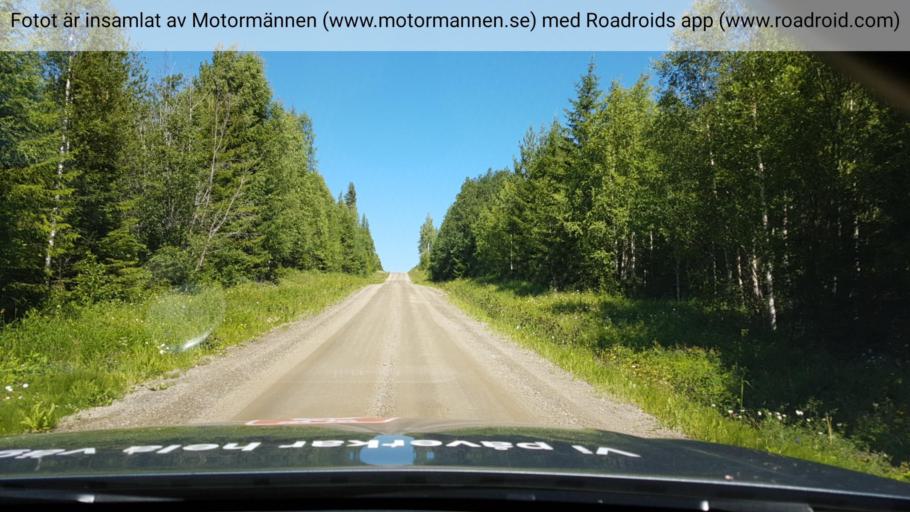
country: SE
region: Jaemtland
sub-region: Braecke Kommun
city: Braecke
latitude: 62.8181
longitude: 15.2228
